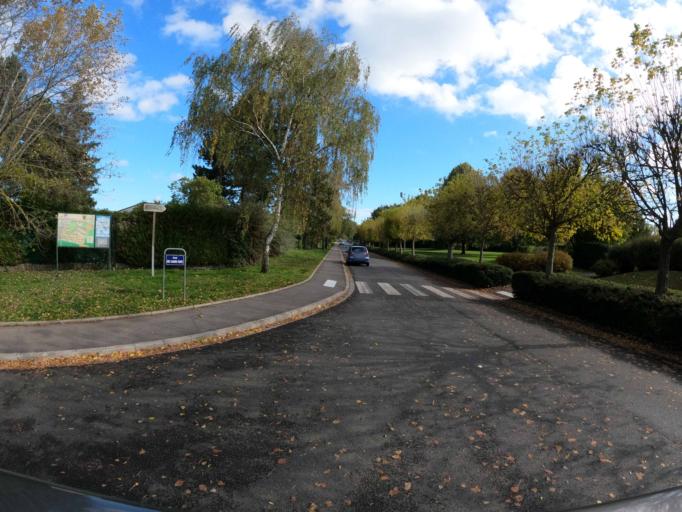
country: FR
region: Ile-de-France
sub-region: Departement de Seine-et-Marne
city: Esbly
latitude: 48.8944
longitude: 2.8111
